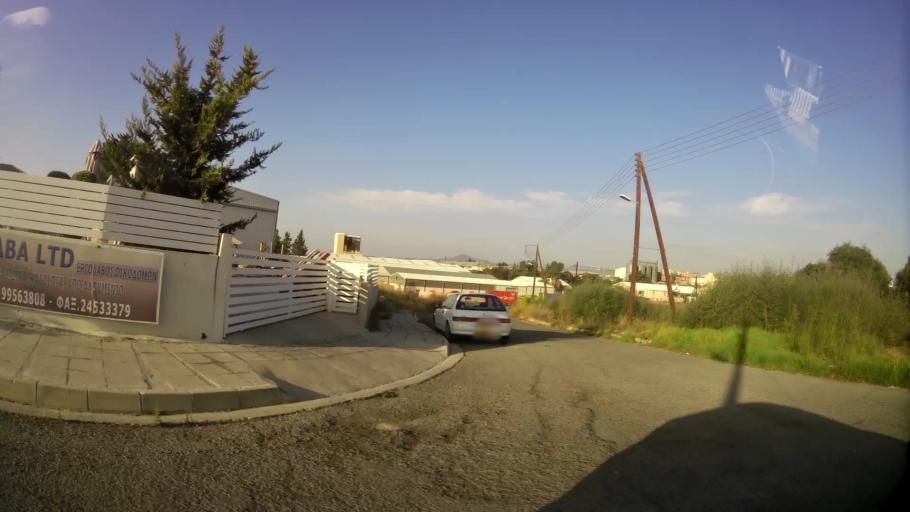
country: CY
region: Larnaka
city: Aradippou
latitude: 34.9314
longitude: 33.5913
